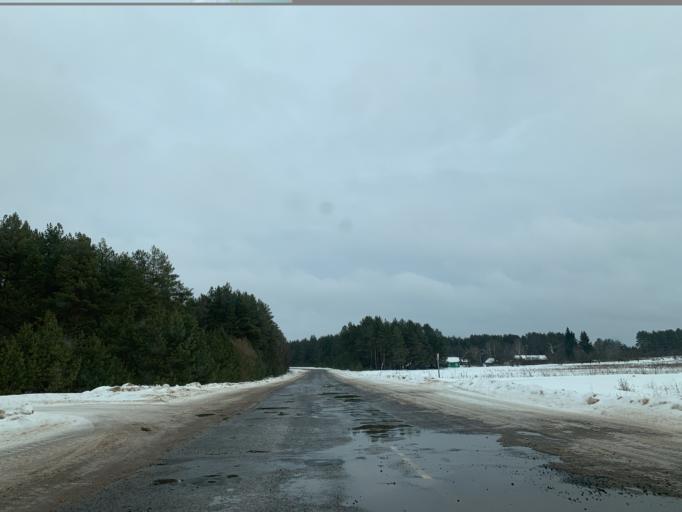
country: BY
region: Minsk
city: Il'ya
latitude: 54.3270
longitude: 27.2500
